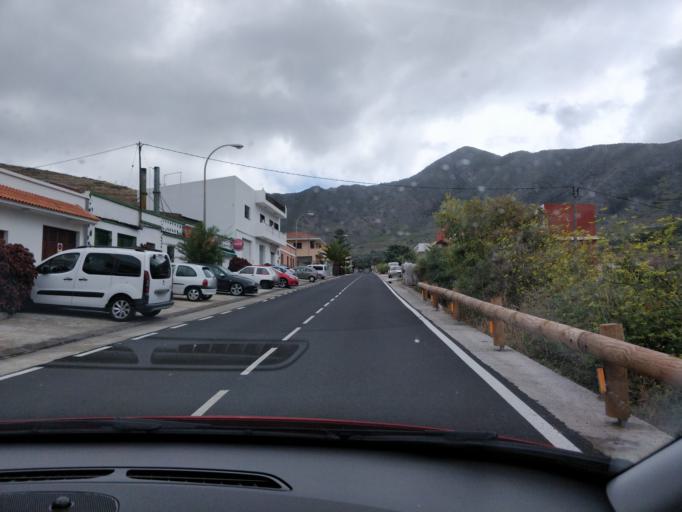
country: ES
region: Canary Islands
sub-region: Provincia de Santa Cruz de Tenerife
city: Tanque
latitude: 28.3441
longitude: -16.8469
